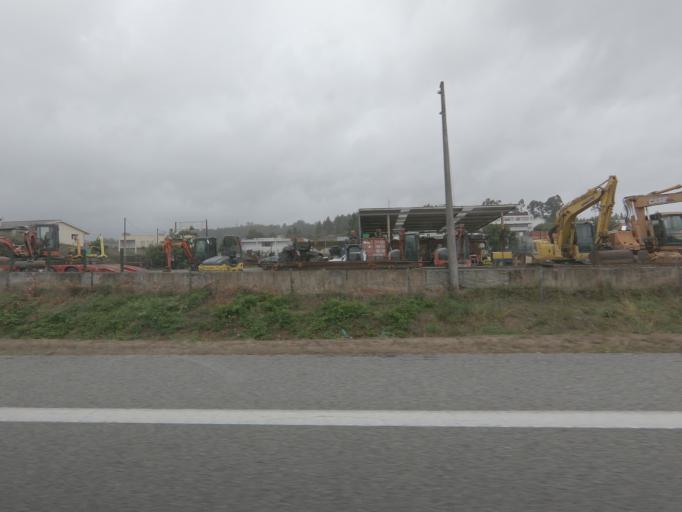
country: PT
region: Porto
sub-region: Lousada
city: Meinedo
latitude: 41.2235
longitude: -8.2363
